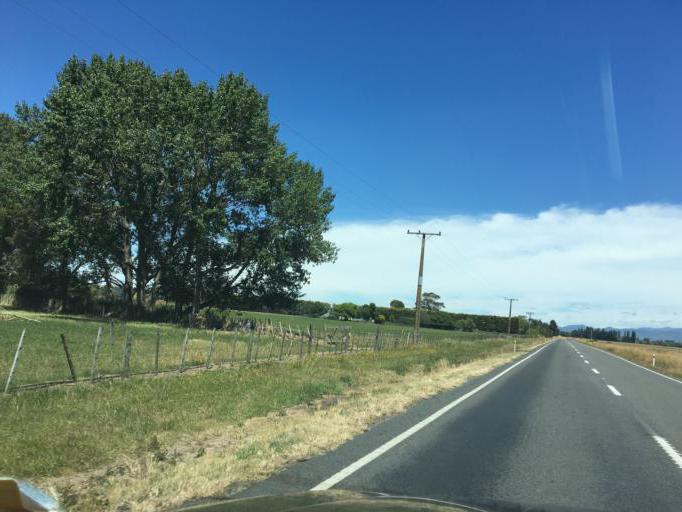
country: NZ
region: Hawke's Bay
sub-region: Hastings District
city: Hastings
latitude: -39.9971
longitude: 176.4170
